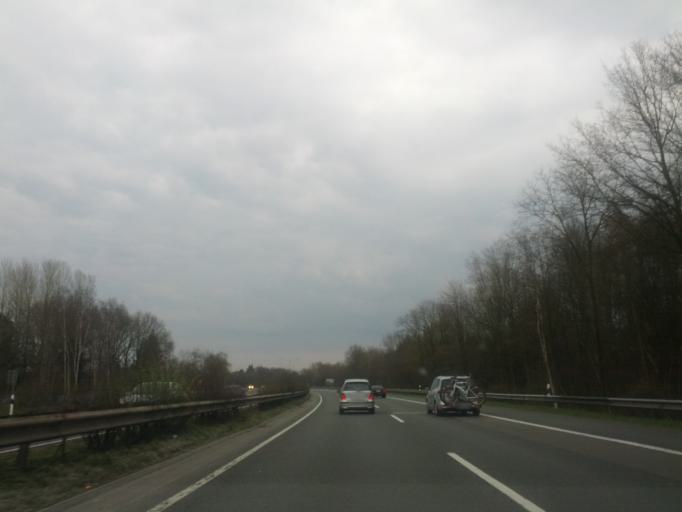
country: DE
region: Lower Saxony
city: Oldenburg
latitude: 53.1617
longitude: 8.1313
